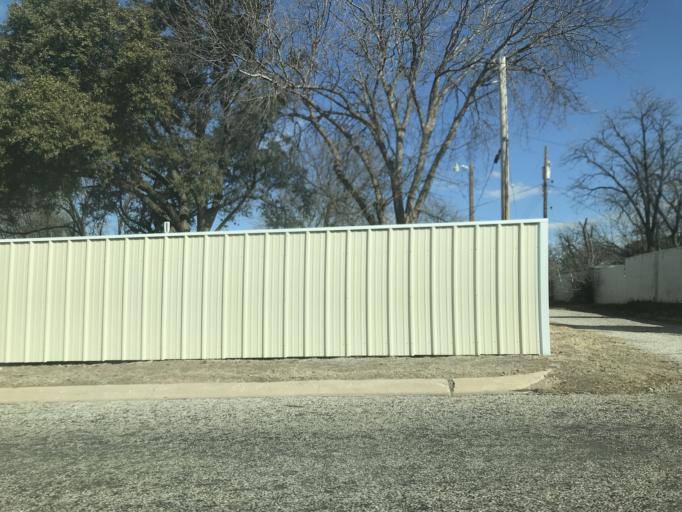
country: US
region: Texas
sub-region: Tom Green County
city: San Angelo
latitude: 31.4434
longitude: -100.4734
